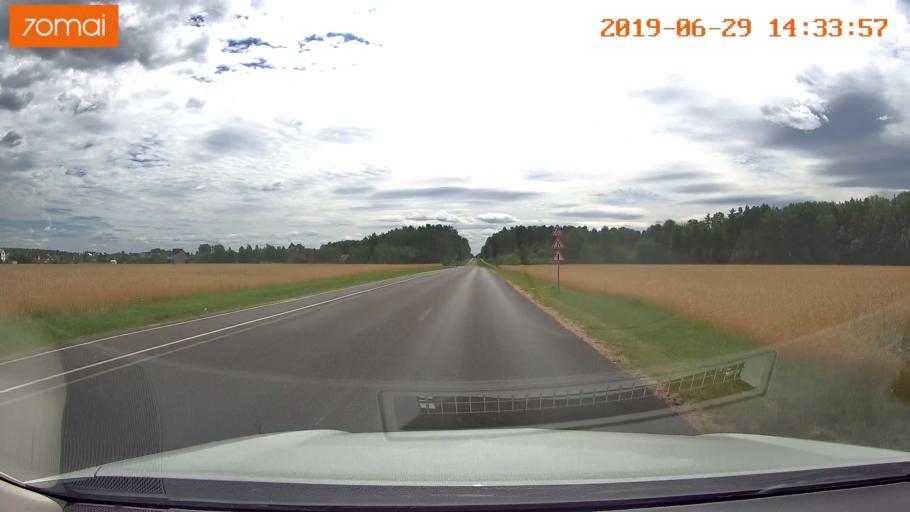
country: BY
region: Minsk
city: Salihorsk
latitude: 52.7730
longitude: 27.4969
